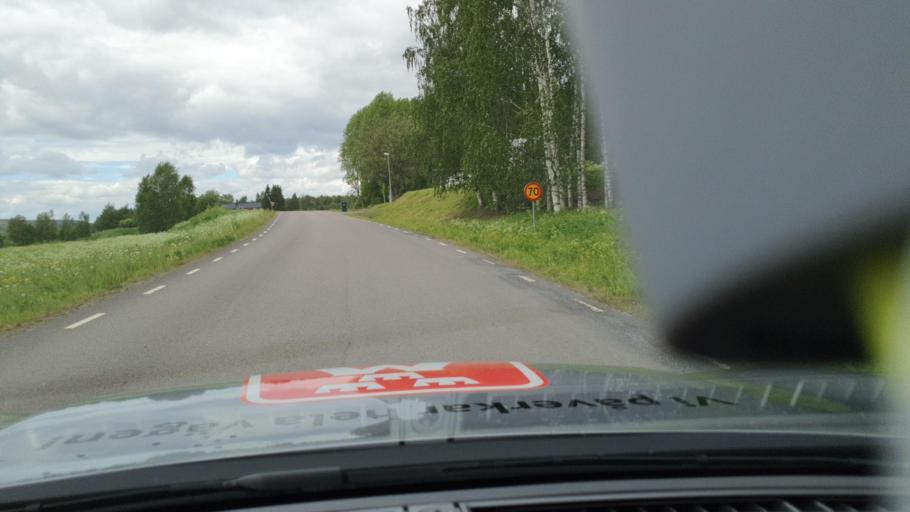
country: SE
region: Norrbotten
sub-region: Lulea Kommun
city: Sodra Sunderbyn
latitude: 65.8340
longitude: 21.9522
